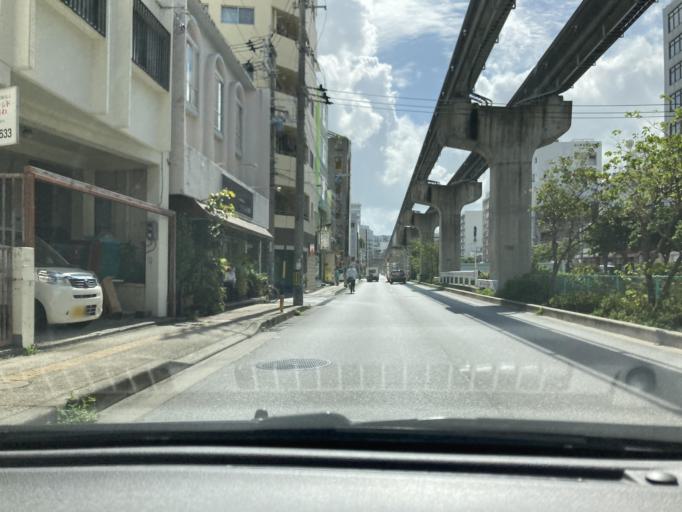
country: JP
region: Okinawa
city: Naha-shi
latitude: 26.2180
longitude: 127.6830
